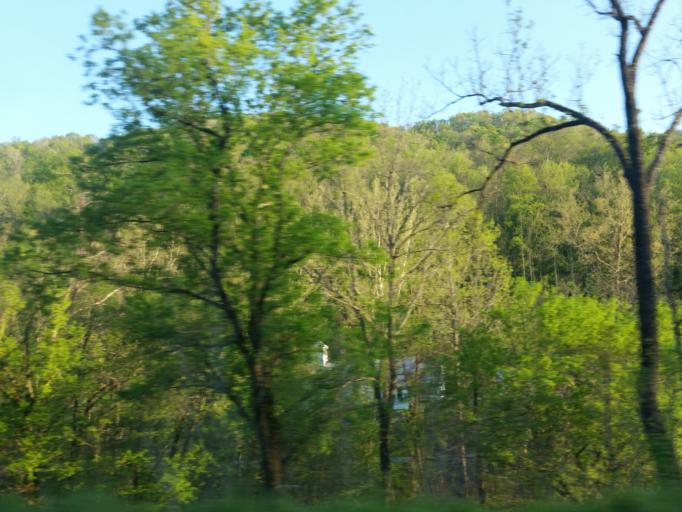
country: US
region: Tennessee
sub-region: Campbell County
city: Jellico
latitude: 36.5468
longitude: -83.9919
